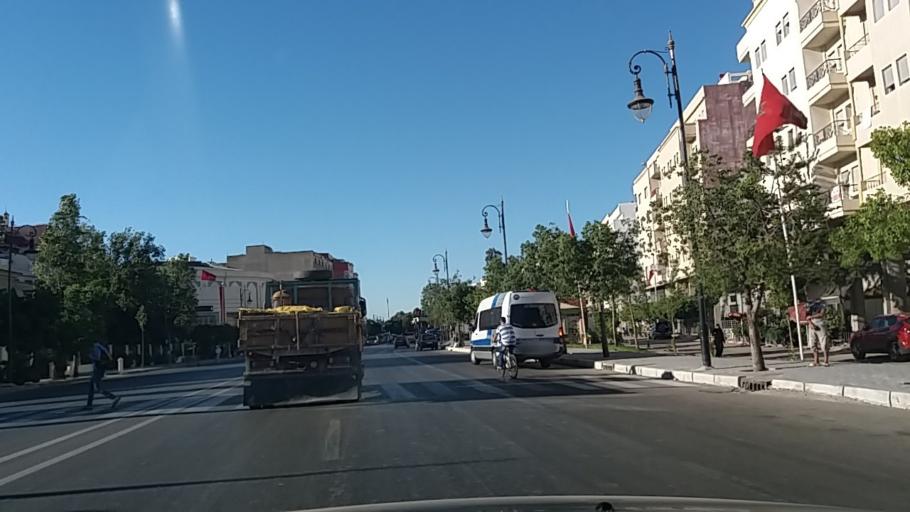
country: MA
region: Tanger-Tetouan
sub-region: Tanger-Assilah
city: Tangier
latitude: 35.7442
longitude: -5.7991
